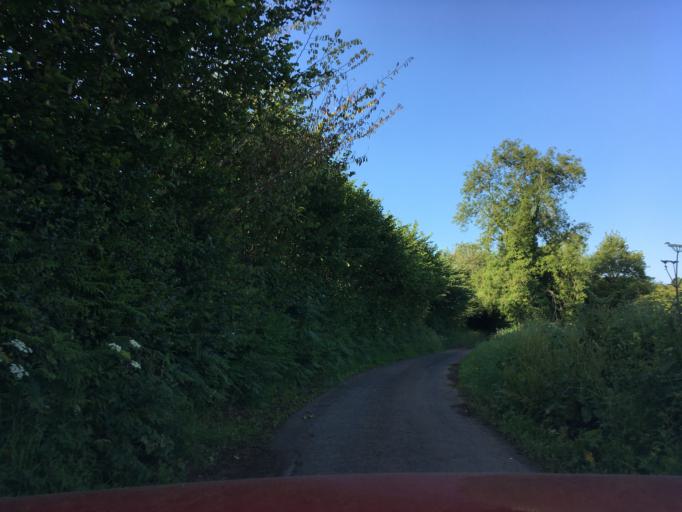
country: GB
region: England
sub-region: Gloucestershire
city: Coleford
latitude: 51.7760
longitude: -2.6276
